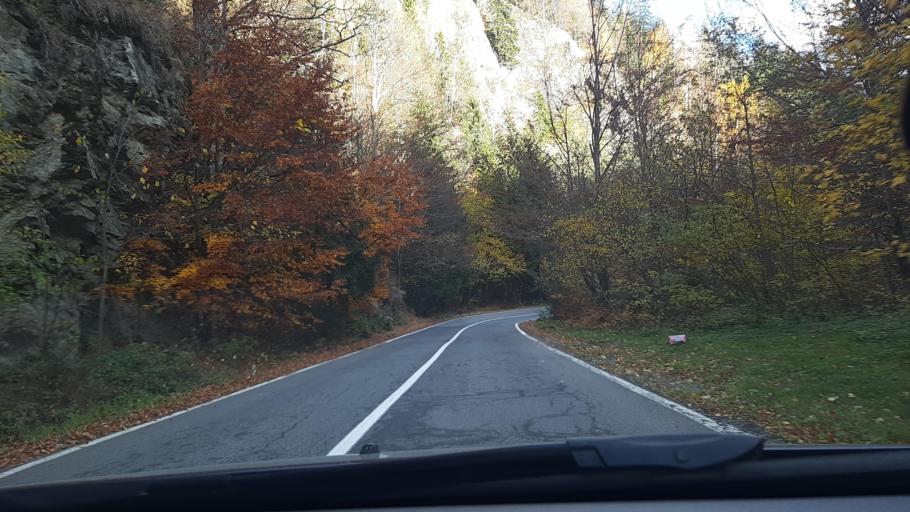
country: RO
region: Valcea
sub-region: Comuna Voineasa
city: Voineasa
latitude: 45.4368
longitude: 23.8628
